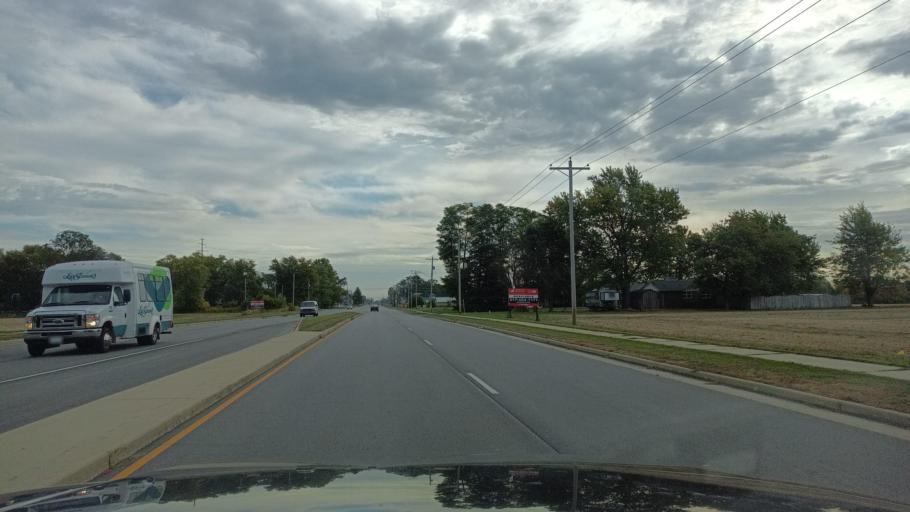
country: US
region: Indiana
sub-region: Delaware County
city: Yorktown
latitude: 40.1812
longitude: -85.4680
